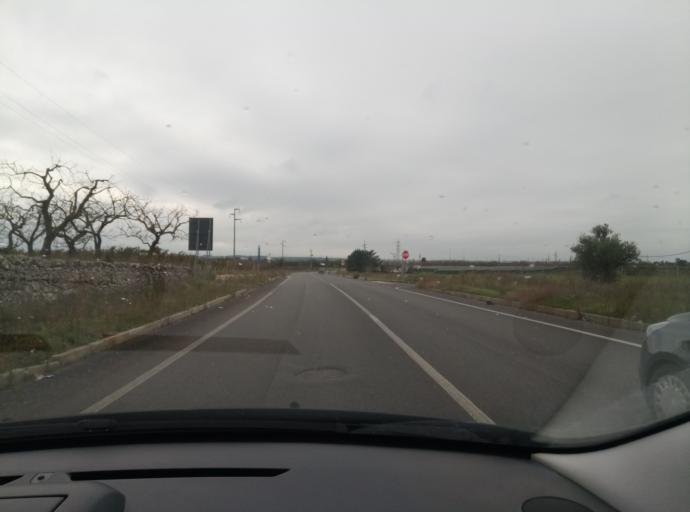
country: IT
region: Apulia
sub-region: Provincia di Bari
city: Acquaviva delle Fonti
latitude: 40.8920
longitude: 16.8313
